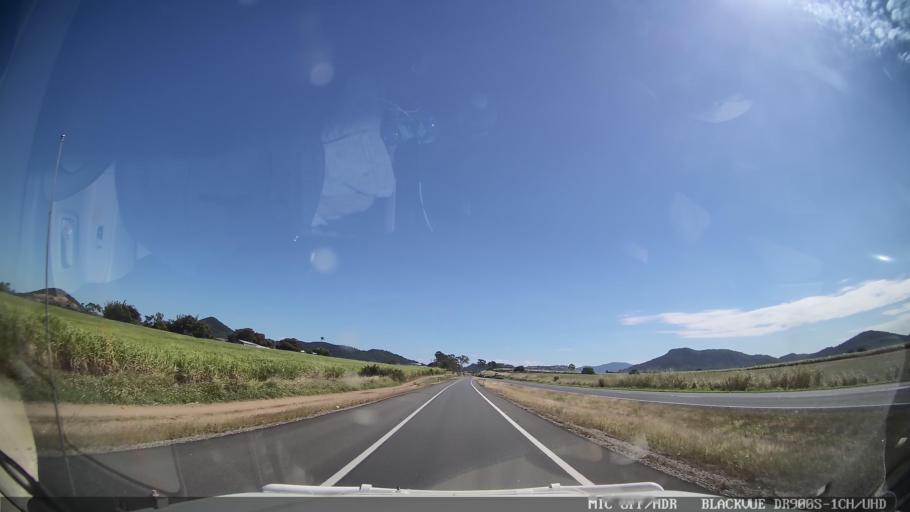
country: AU
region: Queensland
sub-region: Mackay
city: Walkerston
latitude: -21.0913
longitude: 149.0563
